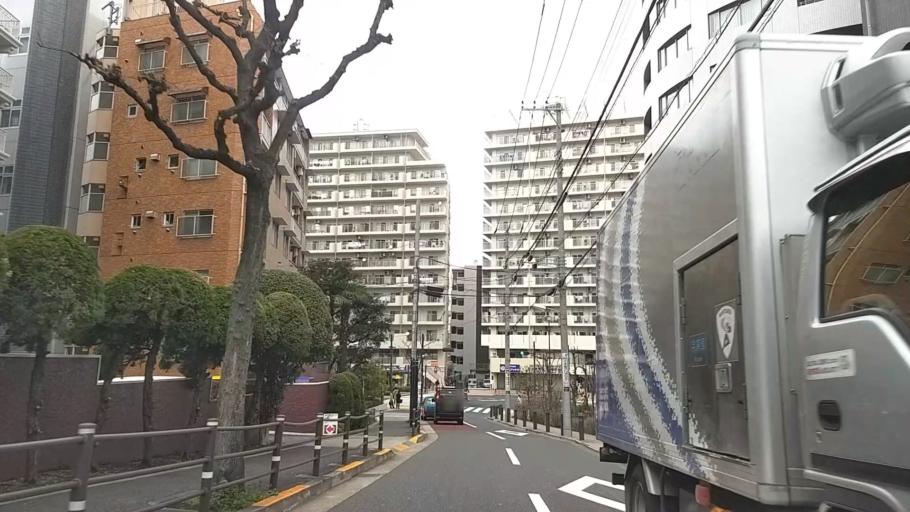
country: JP
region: Tokyo
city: Tokyo
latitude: 35.6211
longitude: 139.7242
